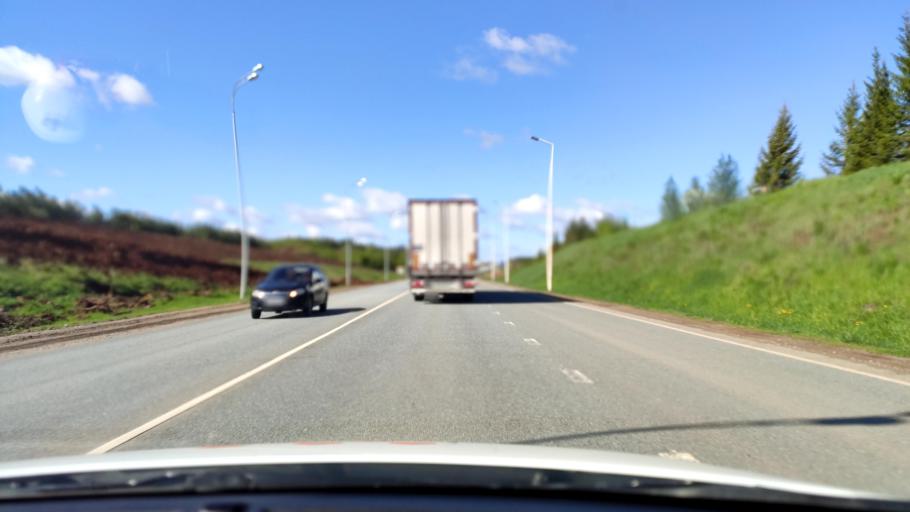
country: RU
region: Tatarstan
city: Sviyazhsk
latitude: 55.7313
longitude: 48.7715
